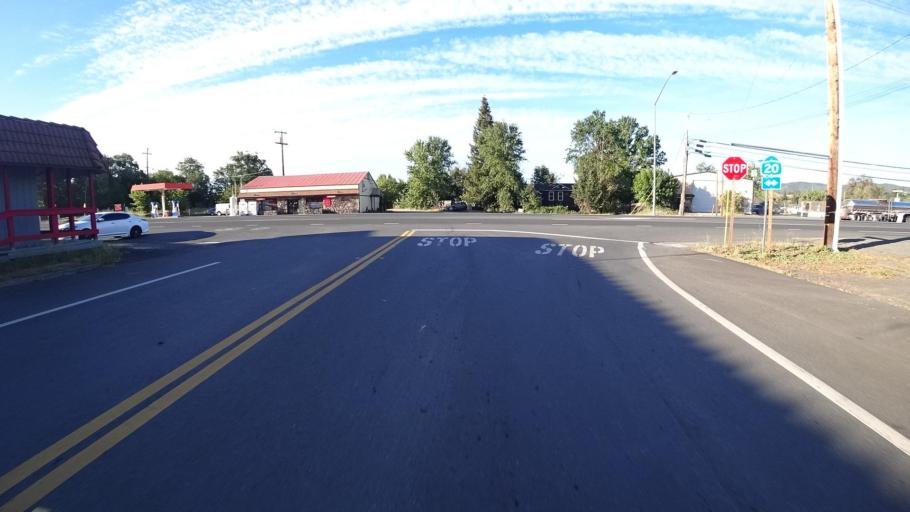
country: US
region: California
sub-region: Lake County
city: Upper Lake
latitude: 39.1626
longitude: -122.9124
